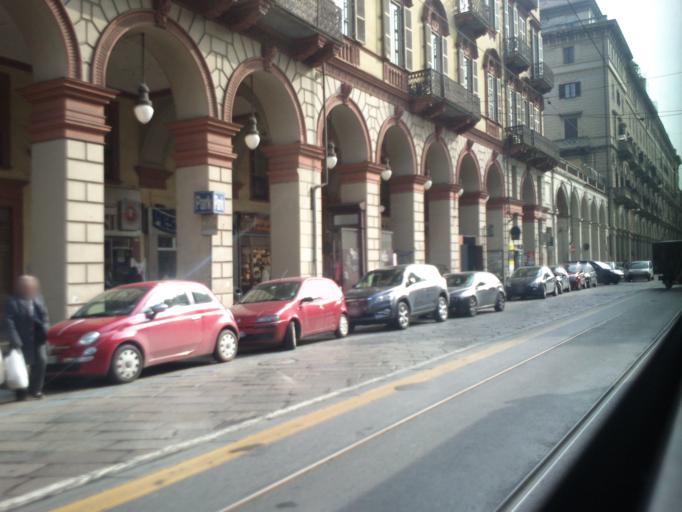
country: IT
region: Piedmont
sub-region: Provincia di Torino
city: Turin
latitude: 45.0727
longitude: 7.6708
